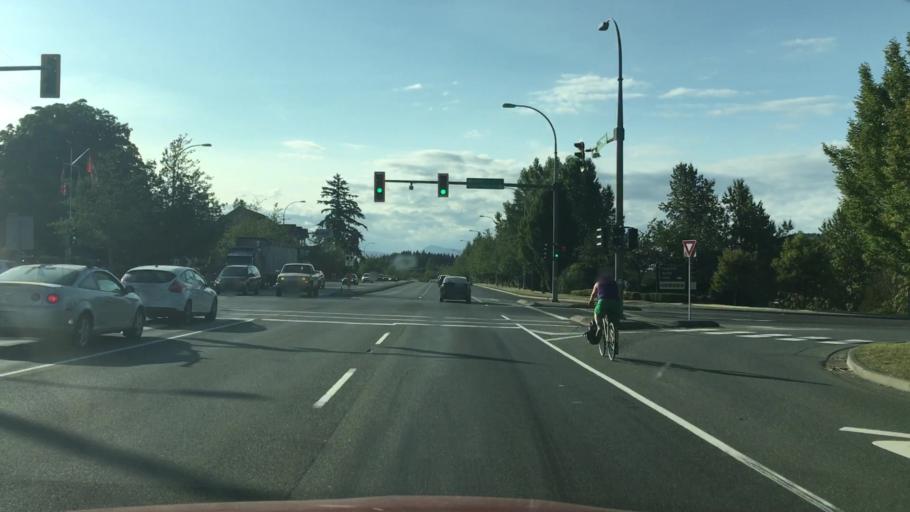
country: CA
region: British Columbia
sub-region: Cowichan Valley Regional District
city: Ladysmith
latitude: 48.9934
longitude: -123.8145
